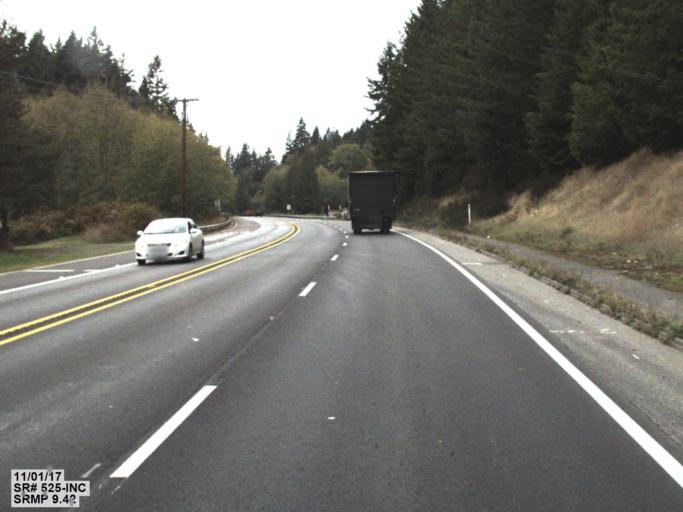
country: US
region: Washington
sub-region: Island County
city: Langley
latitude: 47.9794
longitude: -122.3684
